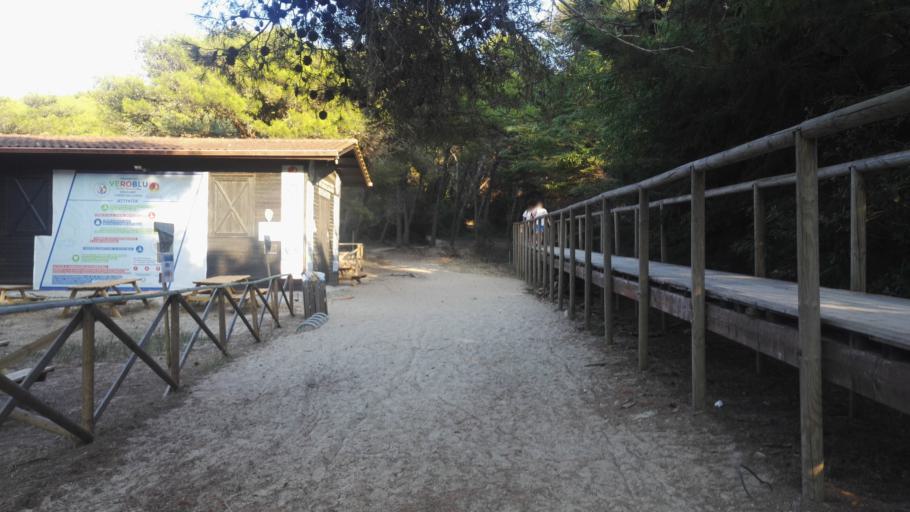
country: IT
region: Apulia
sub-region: Provincia di Lecce
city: Borgagne
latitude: 40.2684
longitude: 18.4322
